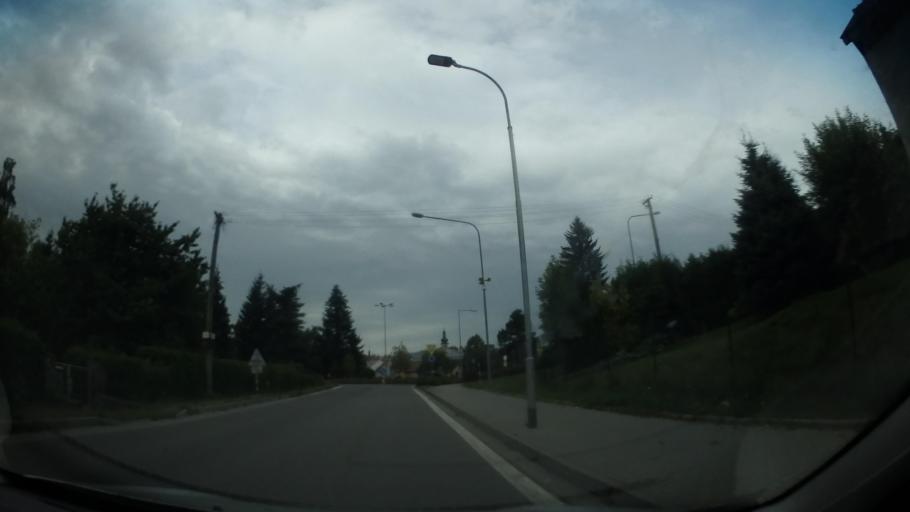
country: CZ
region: Vysocina
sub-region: Okres Zd'ar nad Sazavou
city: Nove Mesto na Morave
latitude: 49.5570
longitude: 16.0730
